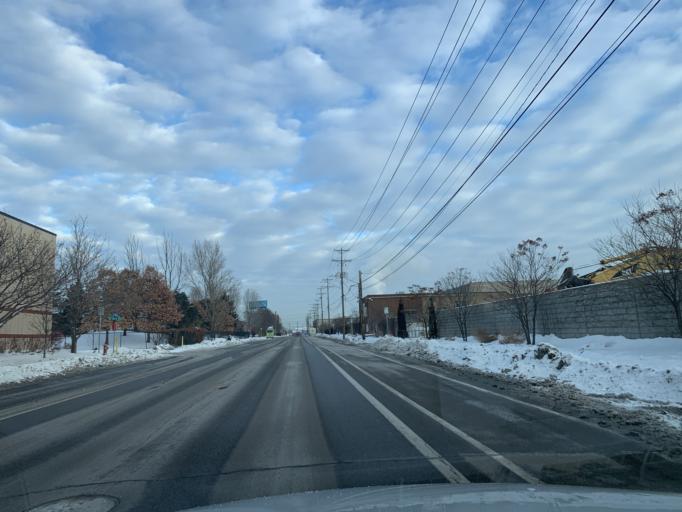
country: US
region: Minnesota
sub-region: Hennepin County
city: Minneapolis
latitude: 44.9938
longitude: -93.2799
